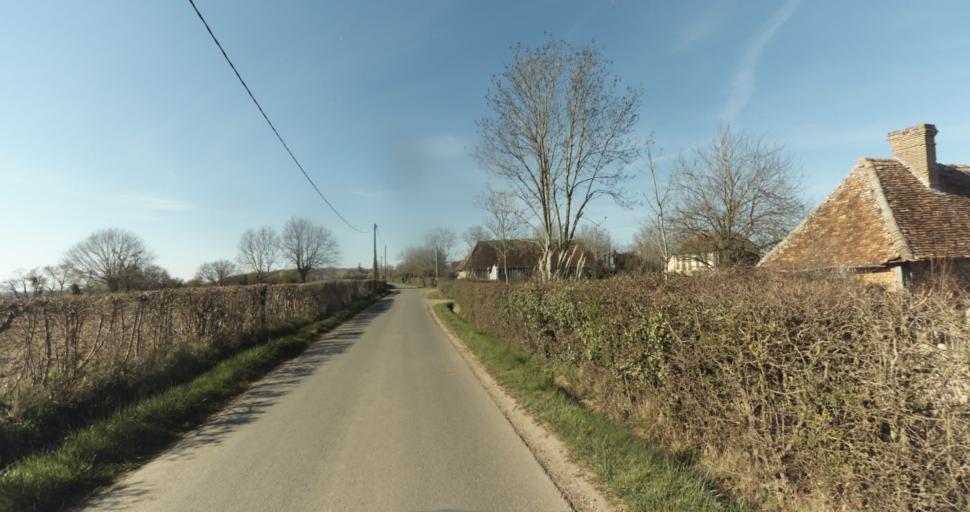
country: FR
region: Lower Normandy
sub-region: Departement du Calvados
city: Saint-Pierre-sur-Dives
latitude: 49.0328
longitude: 0.0553
